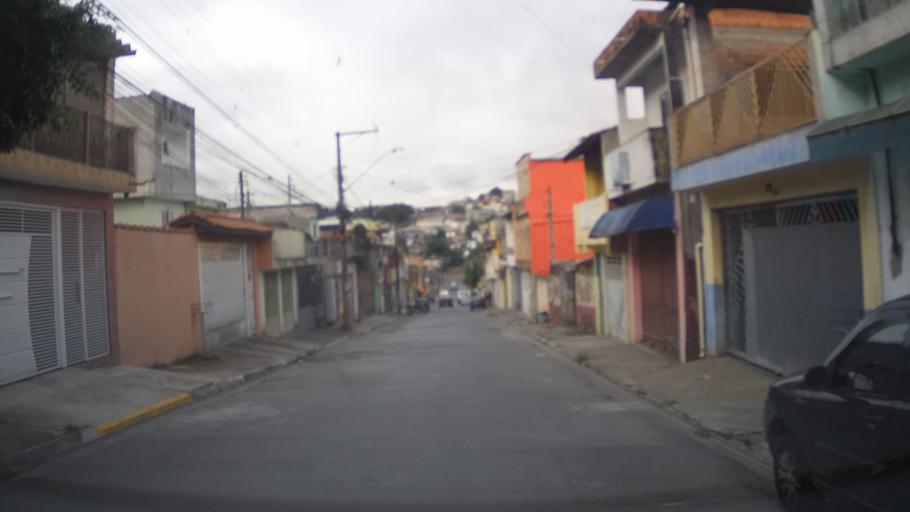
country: BR
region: Sao Paulo
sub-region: Itaquaquecetuba
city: Itaquaquecetuba
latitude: -23.4473
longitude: -46.4217
